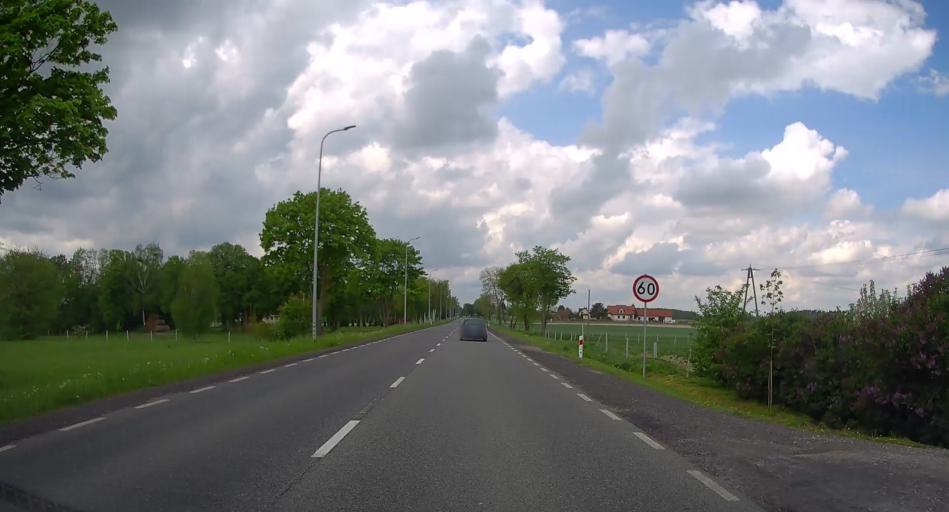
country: PL
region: Masovian Voivodeship
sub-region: Powiat plonski
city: Zaluski
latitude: 52.4459
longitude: 20.5110
